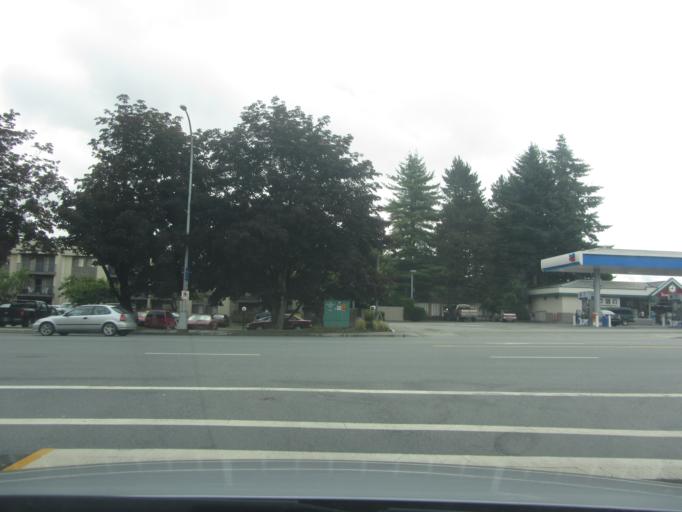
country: CA
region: British Columbia
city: Abbotsford
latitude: 49.0369
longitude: -122.2935
